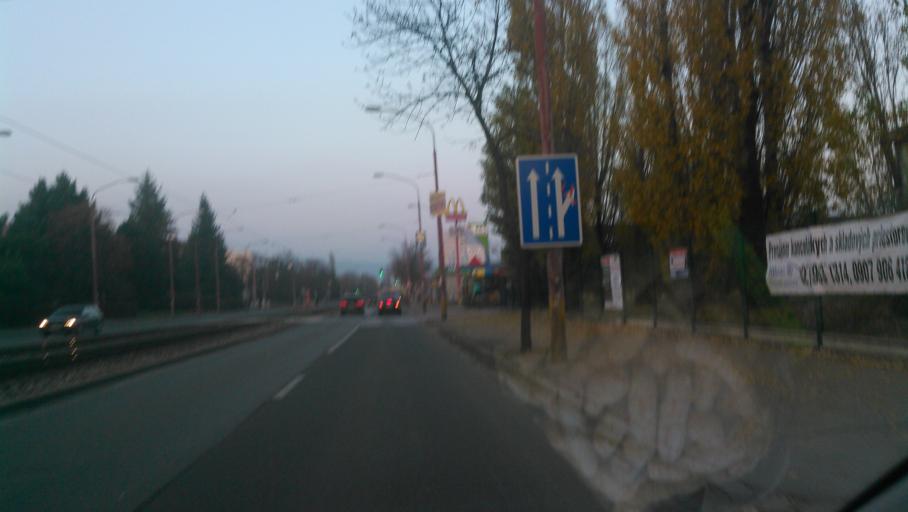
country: SK
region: Bratislavsky
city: Bratislava
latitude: 48.1760
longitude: 17.1279
